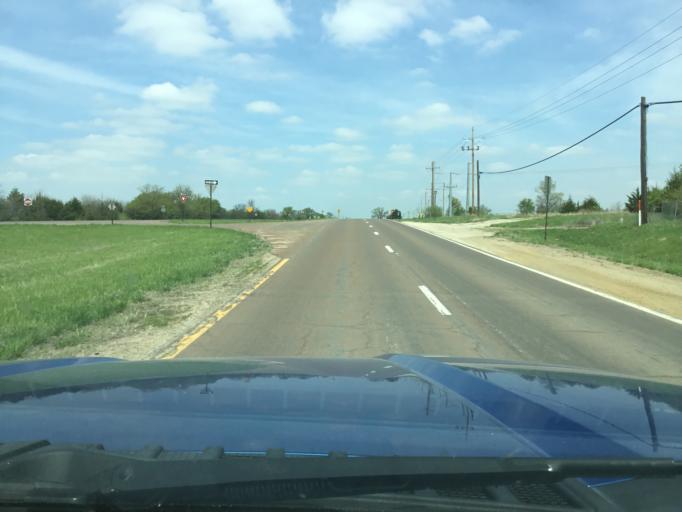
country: US
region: Kansas
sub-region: Osage County
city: Carbondale
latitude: 38.9285
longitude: -95.6876
